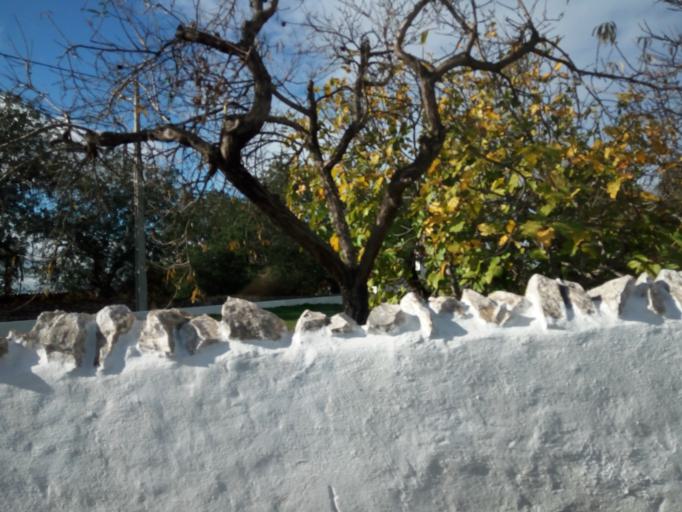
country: PT
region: Faro
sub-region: Faro
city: Santa Barbara de Nexe
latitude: 37.1064
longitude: -7.9618
